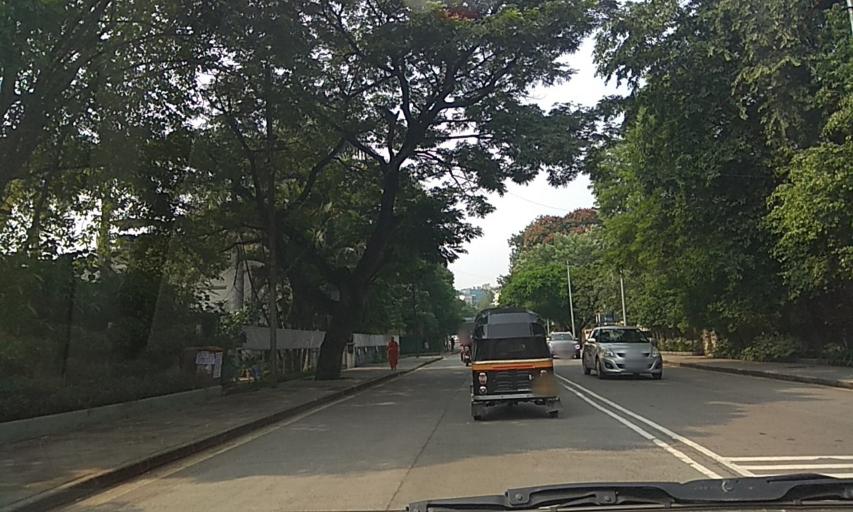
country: IN
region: Maharashtra
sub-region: Pune Division
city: Shivaji Nagar
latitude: 18.5400
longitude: 73.8354
